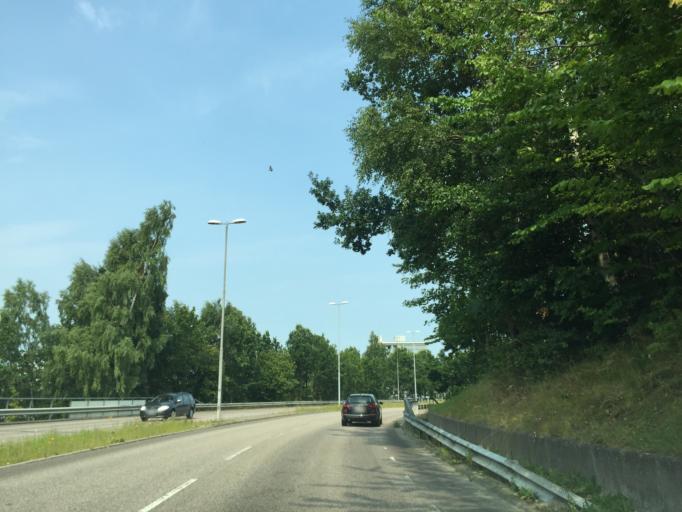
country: SE
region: Skane
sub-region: Angelholms Kommun
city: AEngelholm
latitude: 56.2409
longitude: 12.8669
